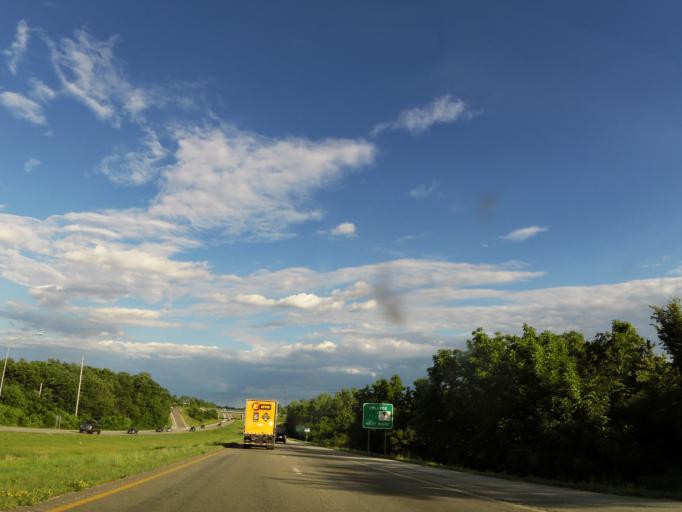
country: US
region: Missouri
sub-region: Saint Charles County
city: Wentzville
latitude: 38.8276
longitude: -90.8530
